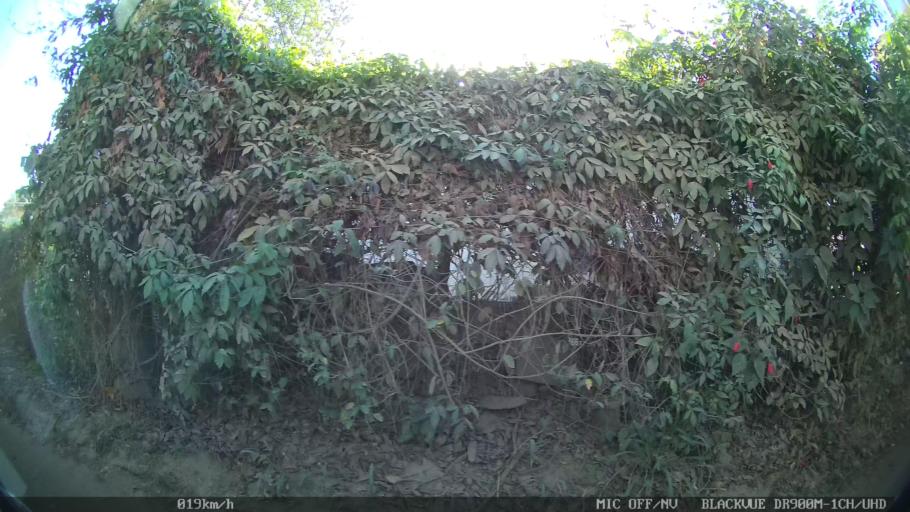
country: BR
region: Sao Paulo
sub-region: Franca
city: Franca
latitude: -20.4821
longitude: -47.4217
